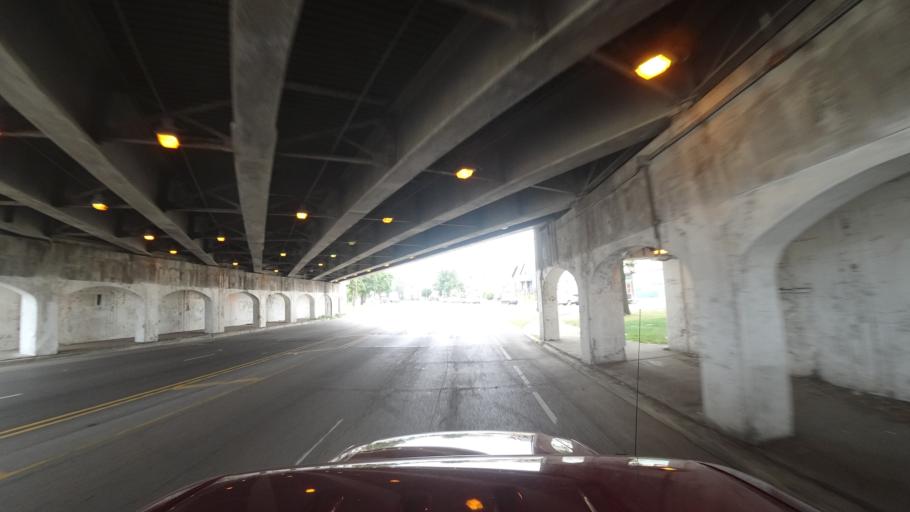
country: US
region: Illinois
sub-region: Cook County
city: Chicago
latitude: 41.8337
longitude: -87.6849
